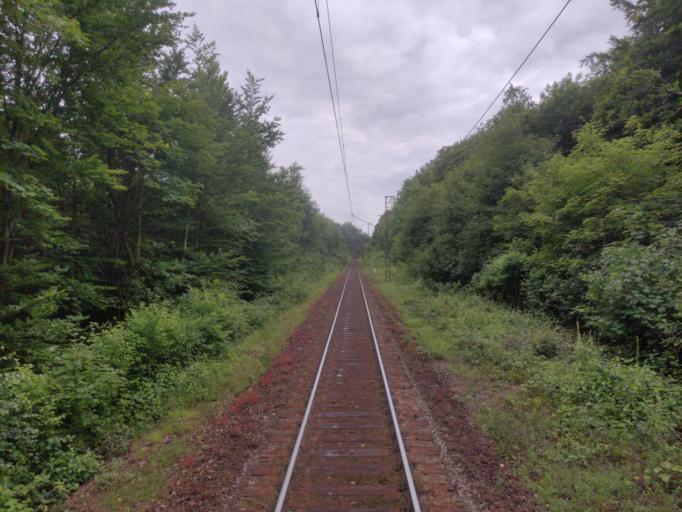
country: DE
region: Saxony-Anhalt
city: Blankenburg
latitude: 51.7955
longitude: 10.9263
